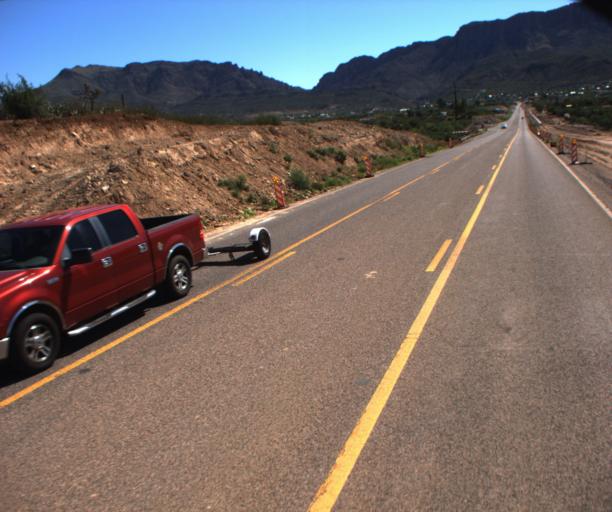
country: US
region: Arizona
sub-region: Pinal County
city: Superior
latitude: 33.2848
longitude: -111.1233
